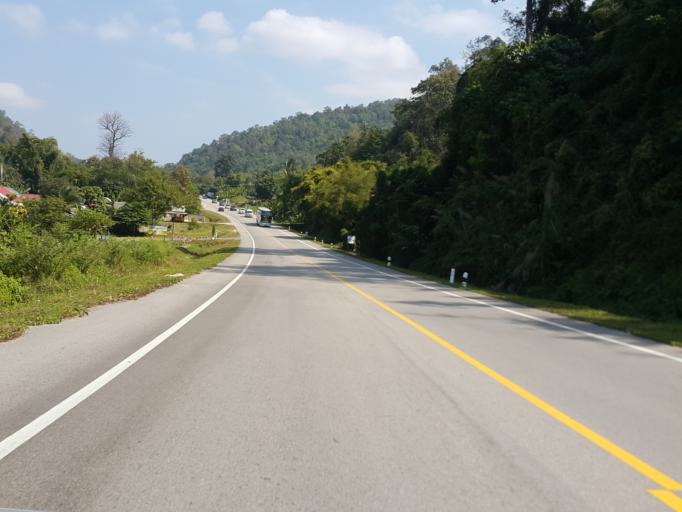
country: TH
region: Chiang Mai
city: Mae On
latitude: 19.0394
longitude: 99.3336
